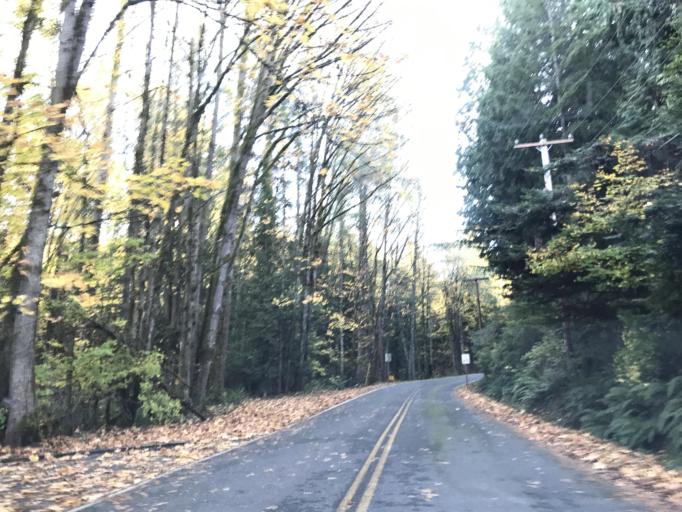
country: US
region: Washington
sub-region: Whatcom County
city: Geneva
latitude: 48.7489
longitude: -122.4102
